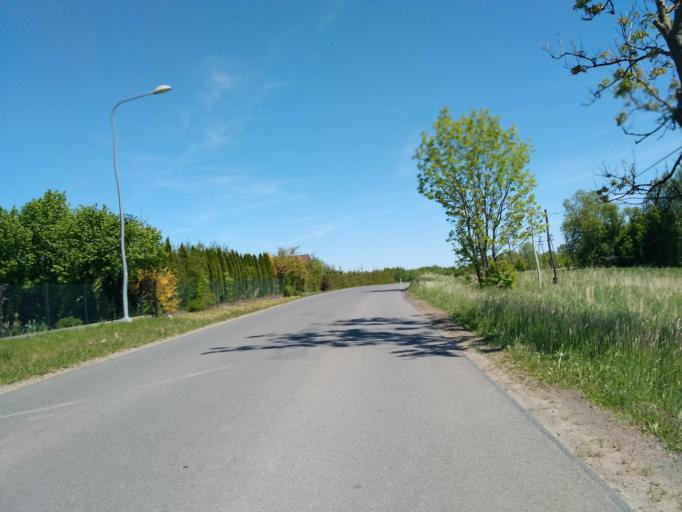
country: PL
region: Subcarpathian Voivodeship
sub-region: Powiat sanocki
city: Nowosielce-Gniewosz
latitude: 49.5514
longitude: 22.0851
